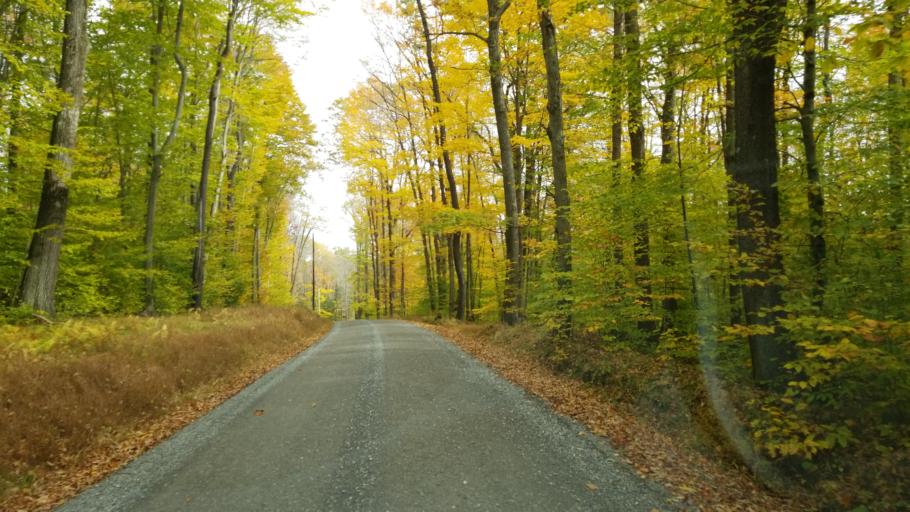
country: US
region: Pennsylvania
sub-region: Clearfield County
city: Clearfield
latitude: 41.1948
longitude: -78.4000
